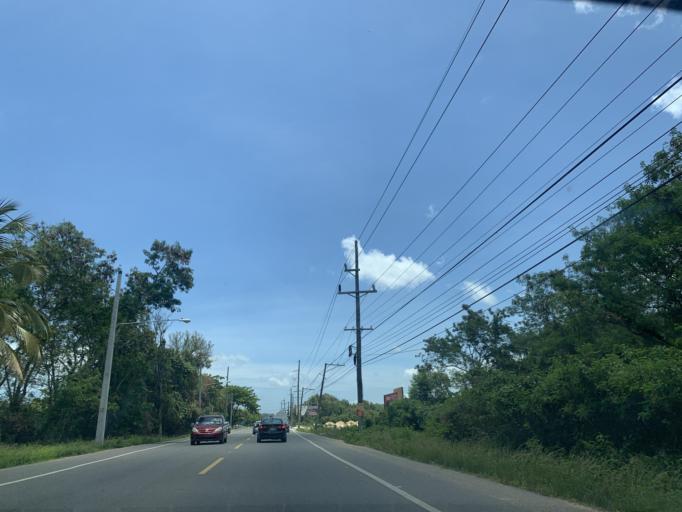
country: DO
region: Puerto Plata
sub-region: Puerto Plata
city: Puerto Plata
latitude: 19.7499
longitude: -70.5651
